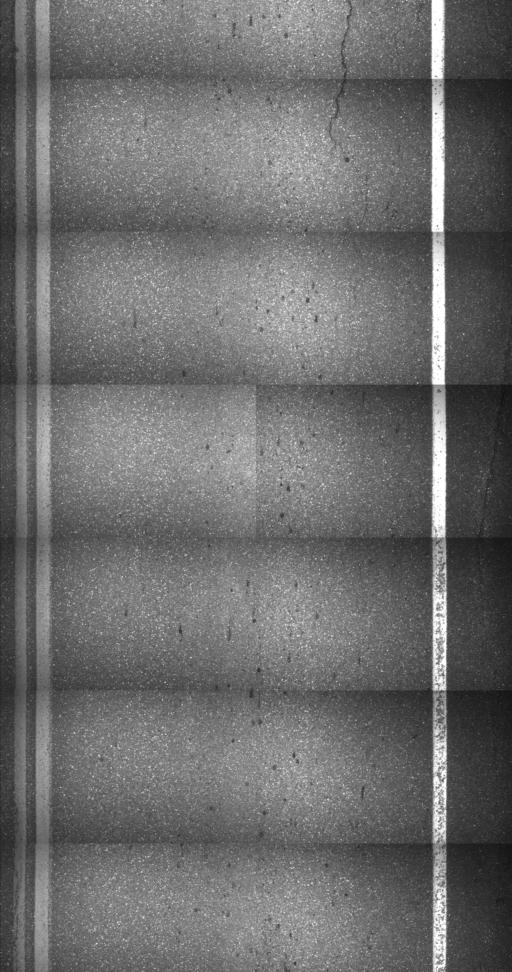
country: US
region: New Hampshire
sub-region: Coos County
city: Stratford
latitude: 44.6498
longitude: -71.5773
